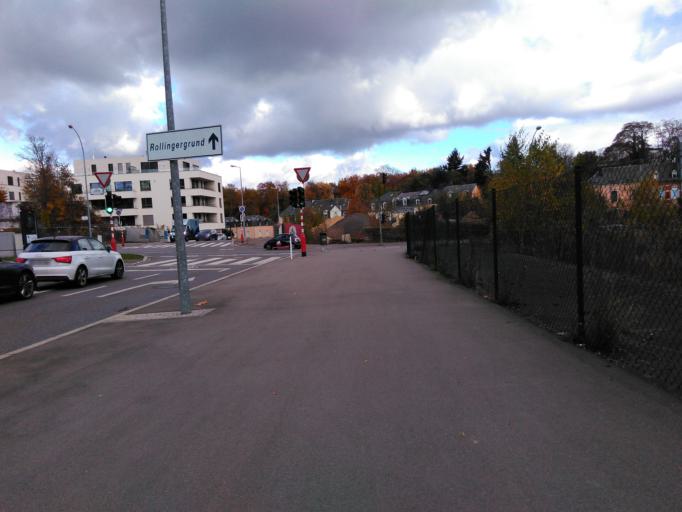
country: LU
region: Luxembourg
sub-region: Canton de Luxembourg
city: Luxembourg
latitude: 49.6132
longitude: 6.1174
